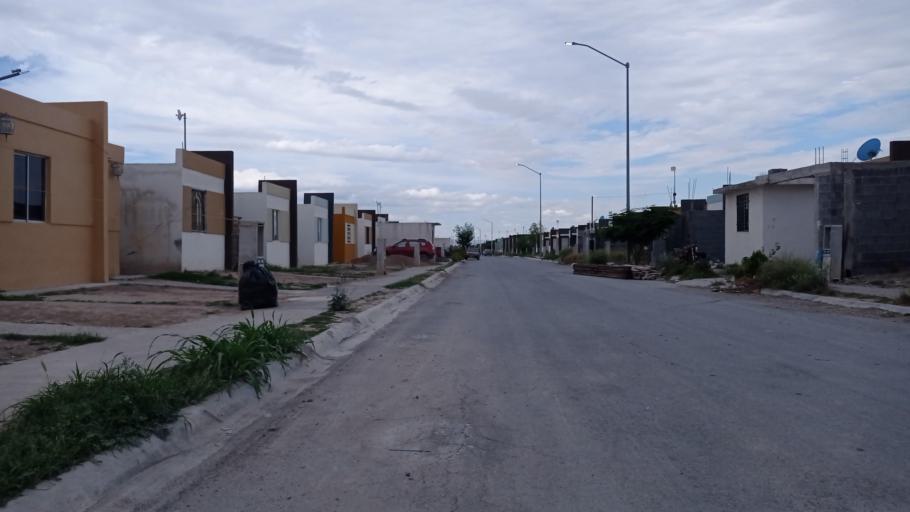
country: MX
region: Nuevo Leon
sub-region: Salinas Victoria
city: Simeprodeso (Colectivo Nuevo)
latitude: 25.8734
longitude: -100.3193
